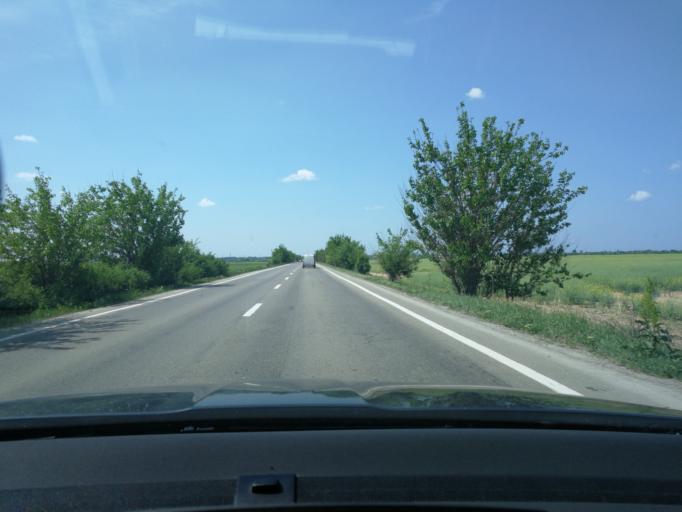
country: RO
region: Prahova
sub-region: Comuna Brazi
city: Negoiesti
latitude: 44.8853
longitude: 25.9527
